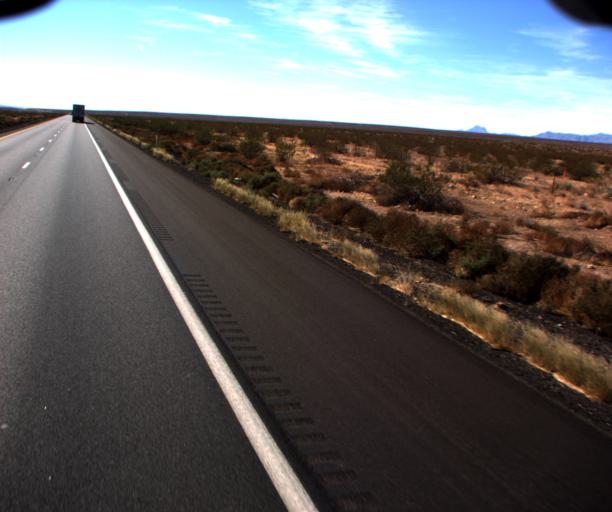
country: US
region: Arizona
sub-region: Mohave County
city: Beaver Dam
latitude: 36.8770
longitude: -113.9532
